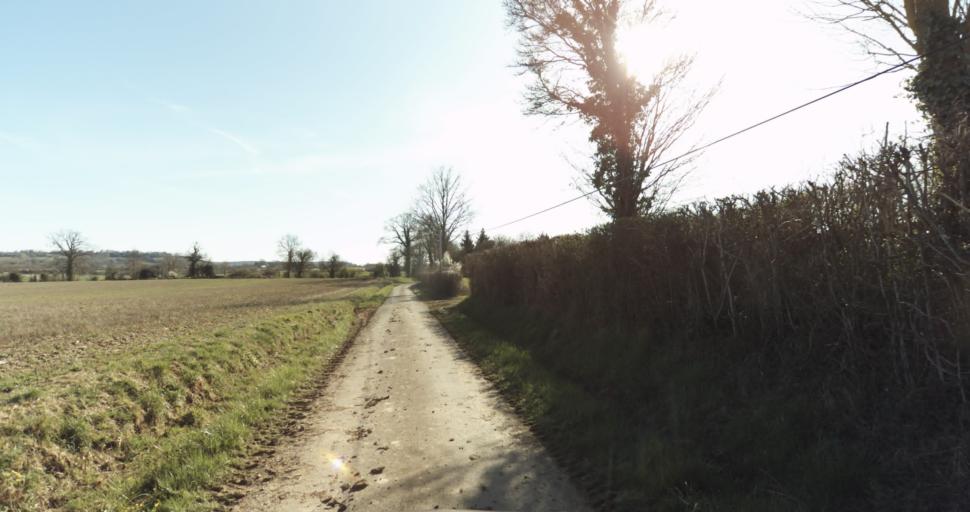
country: FR
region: Lower Normandy
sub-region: Departement du Calvados
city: Livarot
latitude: 49.0563
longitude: 0.0765
